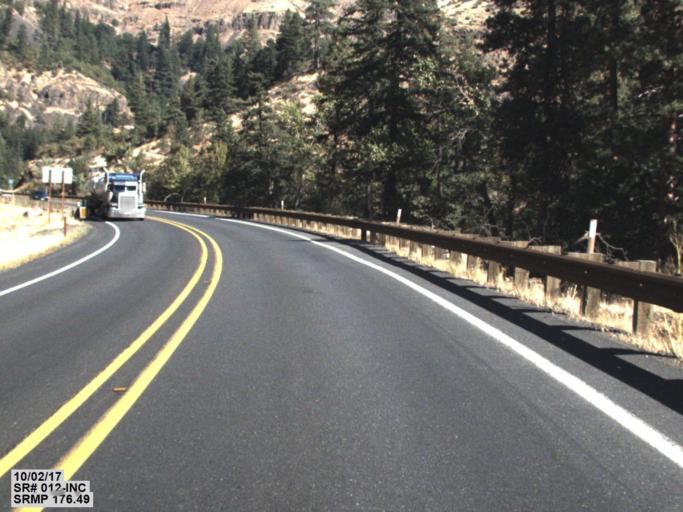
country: US
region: Washington
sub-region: Yakima County
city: Tieton
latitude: 46.6909
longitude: -120.9227
